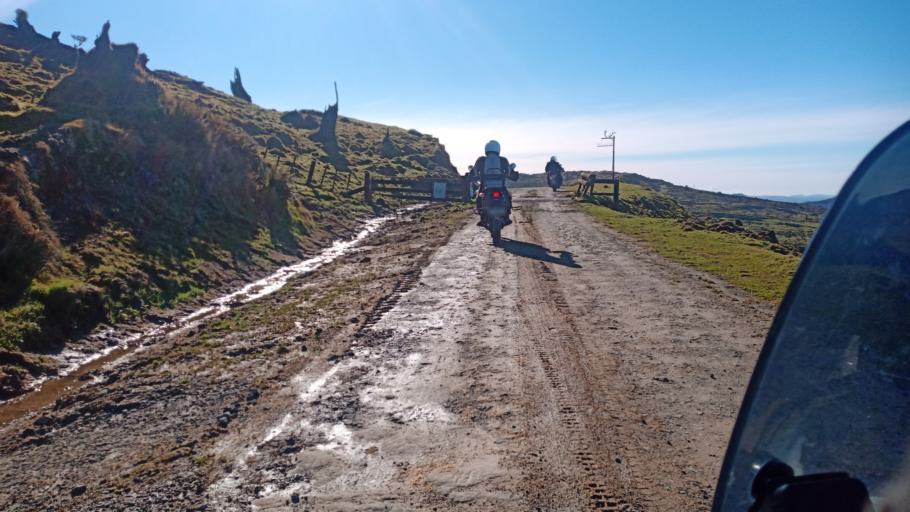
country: NZ
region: Gisborne
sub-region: Gisborne District
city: Gisborne
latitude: -38.1775
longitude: 177.8260
